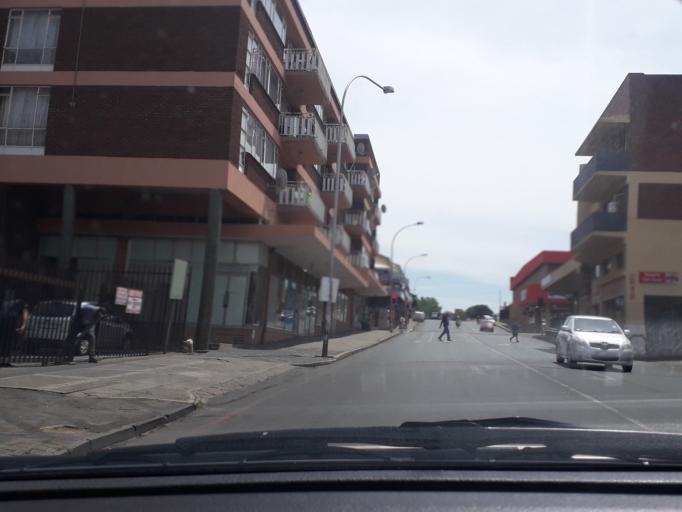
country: ZA
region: Gauteng
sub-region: City of Johannesburg Metropolitan Municipality
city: Roodepoort
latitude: -26.1728
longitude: 27.9109
